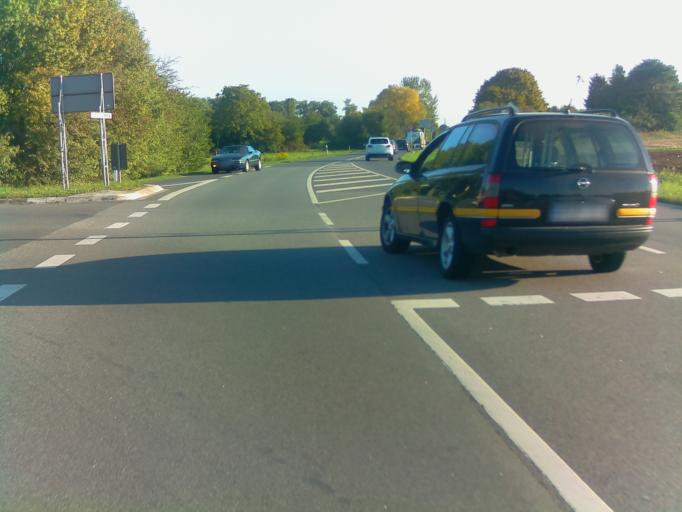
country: DE
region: Hesse
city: Zwingenberg
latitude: 49.7197
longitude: 8.6040
